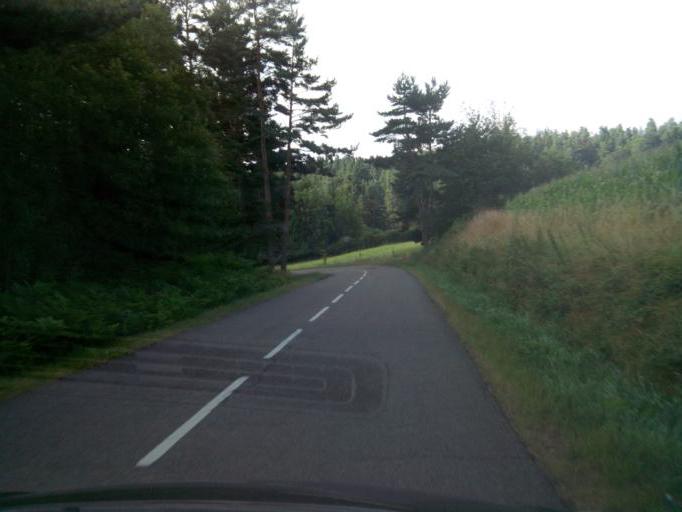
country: FR
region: Rhone-Alpes
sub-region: Departement de la Loire
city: Usson-en-Forez
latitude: 45.3572
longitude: 3.9972
